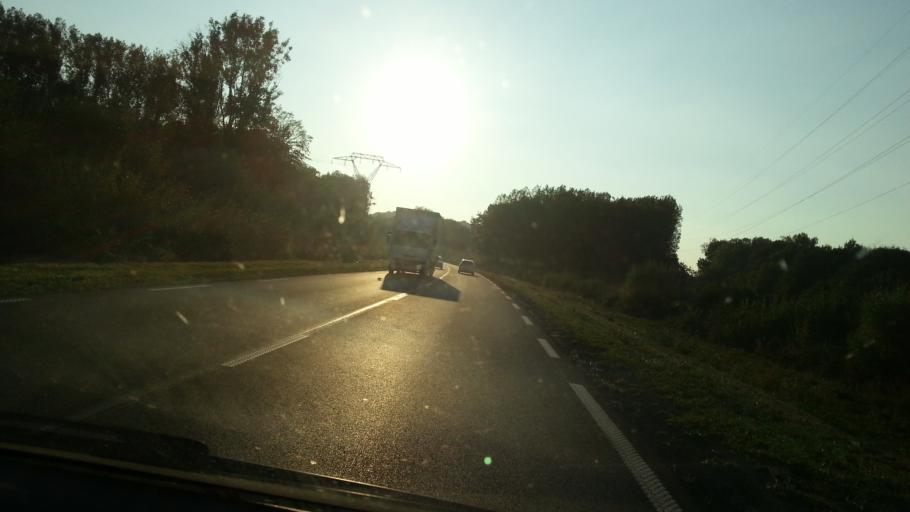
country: FR
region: Picardie
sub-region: Departement de l'Oise
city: Brenouille
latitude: 49.3168
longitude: 2.5639
